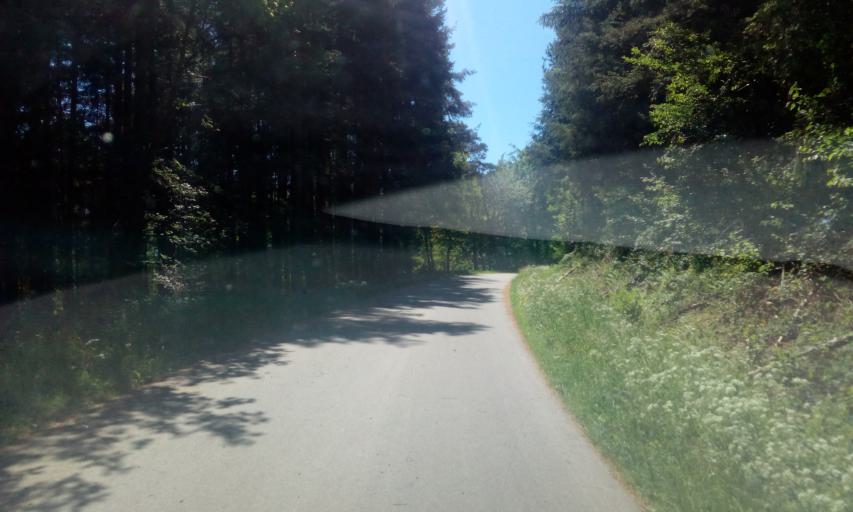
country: DE
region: Rheinland-Pfalz
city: Trittenheim
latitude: 49.8108
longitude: 6.9044
